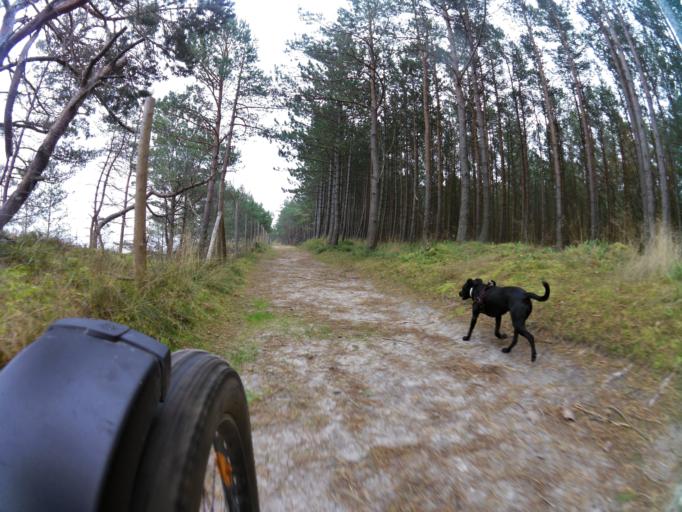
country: PL
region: Pomeranian Voivodeship
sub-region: Powiat pucki
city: Krokowa
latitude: 54.8319
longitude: 18.1039
